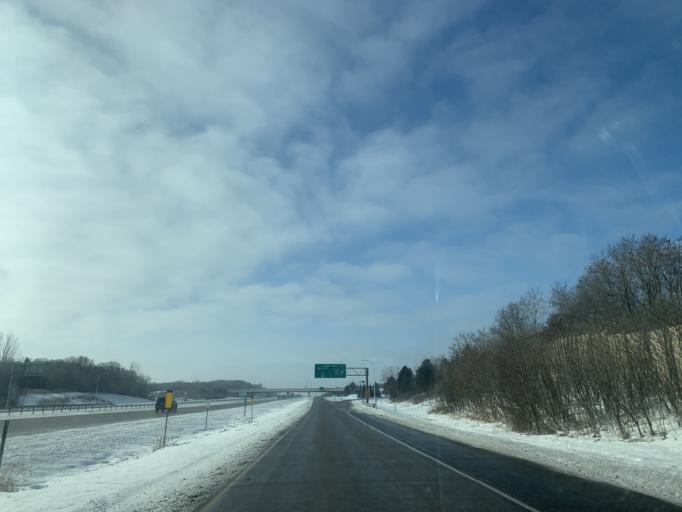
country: US
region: Minnesota
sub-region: Dakota County
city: Eagan
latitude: 44.7827
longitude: -93.2111
